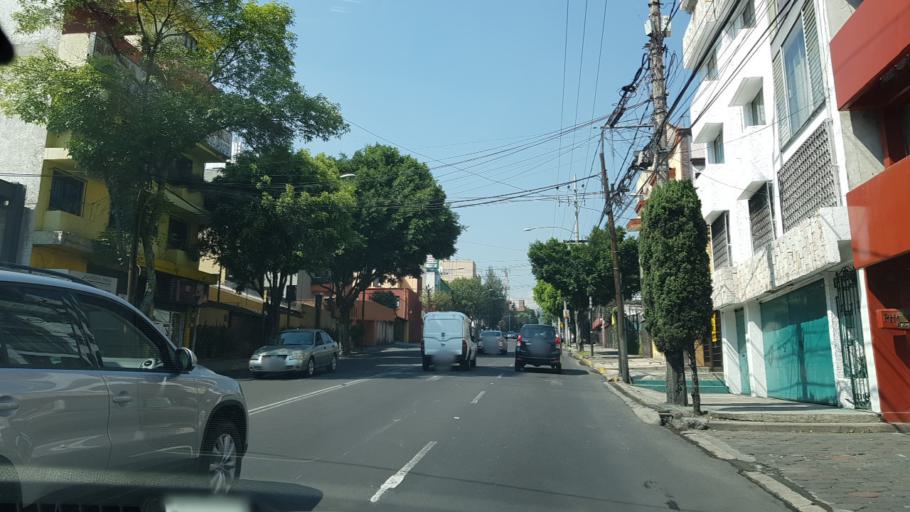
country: MX
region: Mexico City
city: Magdalena Contreras
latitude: 19.3491
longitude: -99.2265
